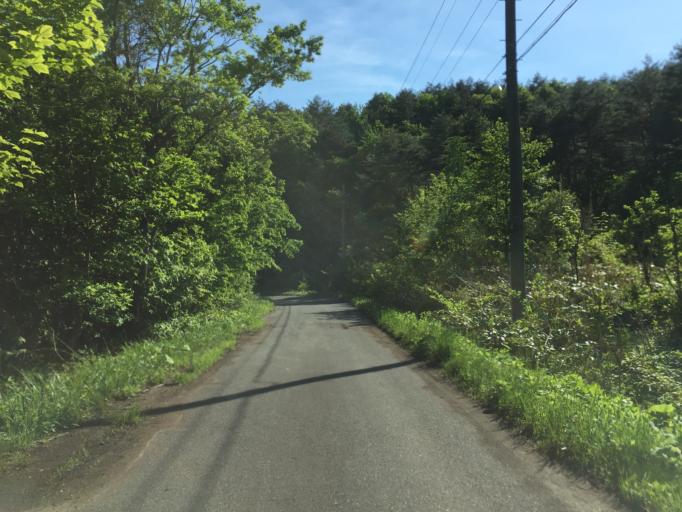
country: JP
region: Fukushima
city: Fukushima-shi
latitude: 37.7272
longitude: 140.3144
